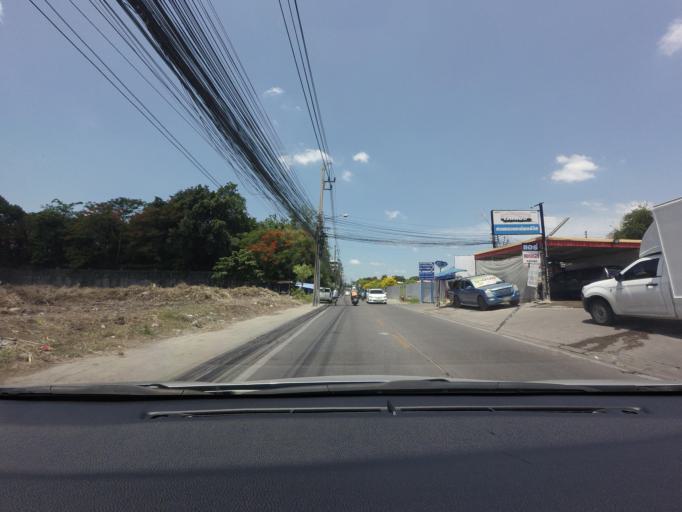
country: TH
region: Bangkok
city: Phra Khanong
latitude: 13.7238
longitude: 100.6154
